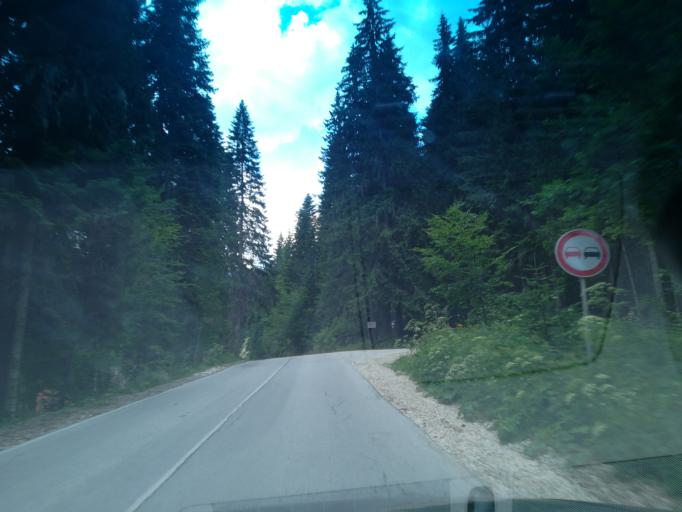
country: BG
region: Smolyan
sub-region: Obshtina Smolyan
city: Smolyan
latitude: 41.6520
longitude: 24.6847
